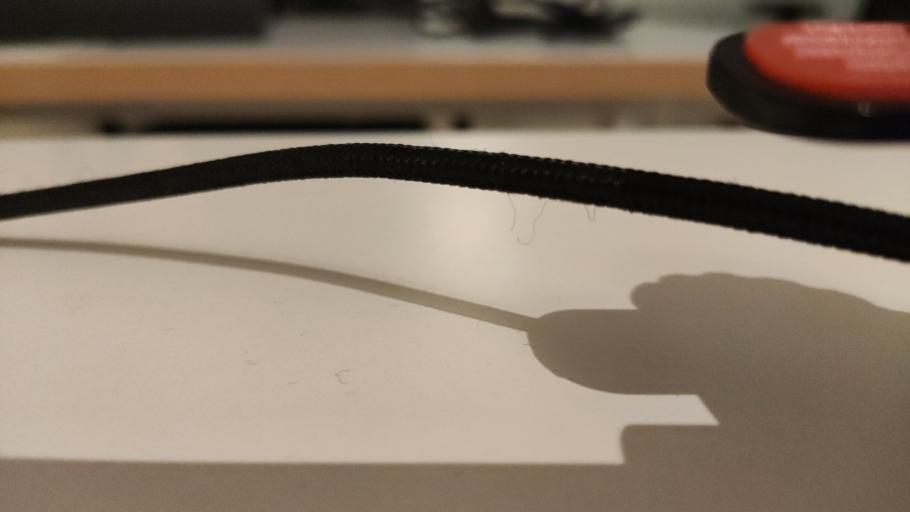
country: RU
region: Moskovskaya
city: Il'inskiy Pogost
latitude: 55.5339
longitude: 38.8726
